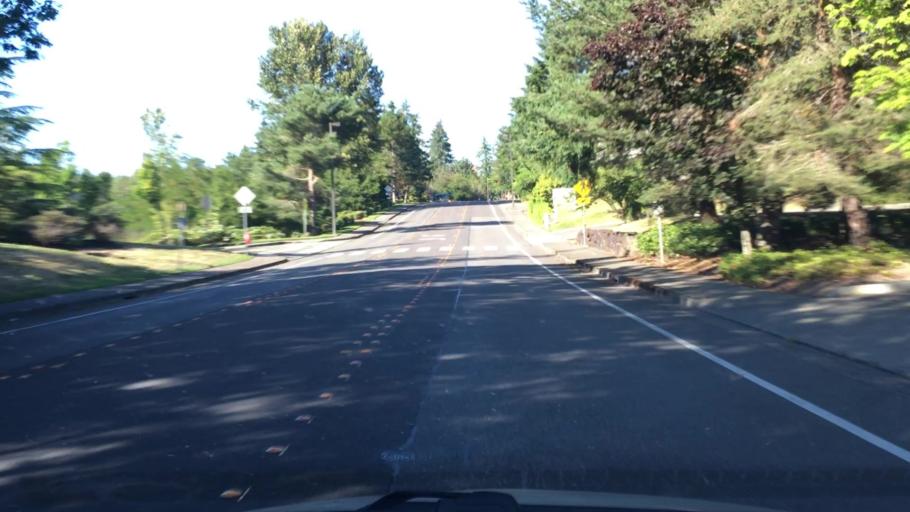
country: US
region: Washington
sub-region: King County
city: Eastgate
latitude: 47.5818
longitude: -122.1296
